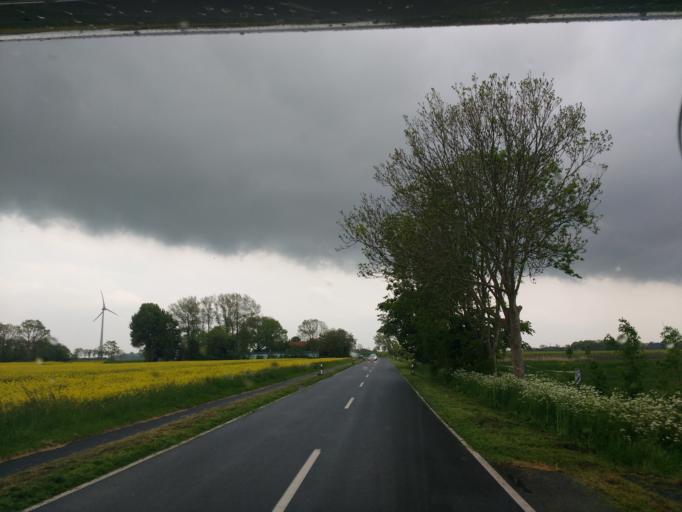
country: DE
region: Lower Saxony
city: Wangerooge
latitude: 53.6962
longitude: 7.8997
